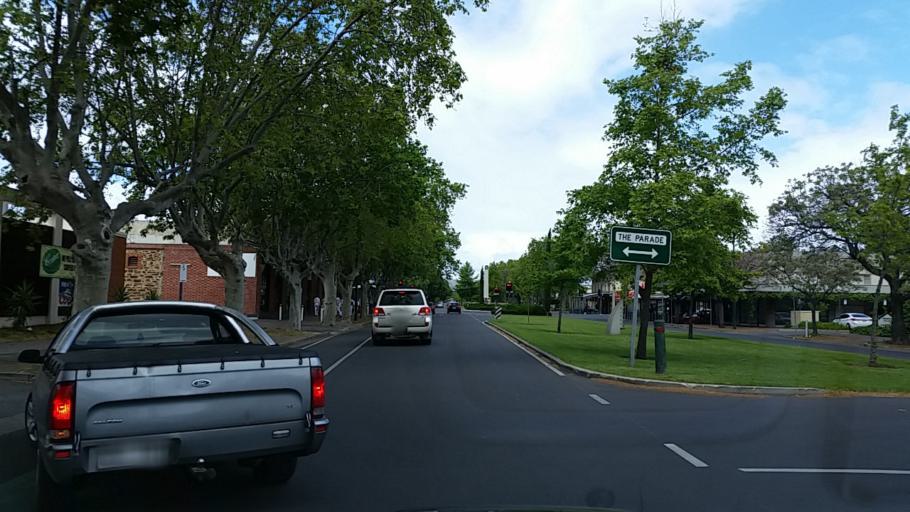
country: AU
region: South Australia
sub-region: Norwood Payneham St Peters
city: Trinity Gardens
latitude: -34.9203
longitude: 138.6321
